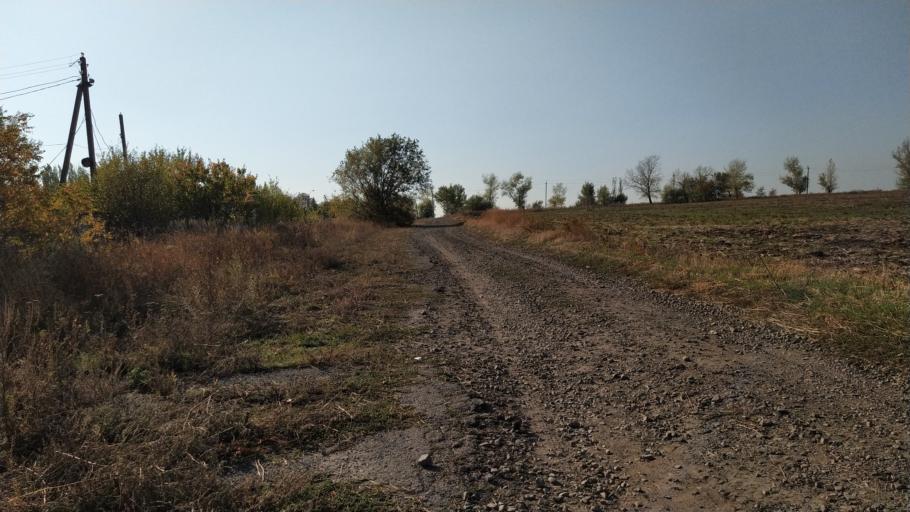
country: RU
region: Rostov
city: Bataysk
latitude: 47.0909
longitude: 39.7764
